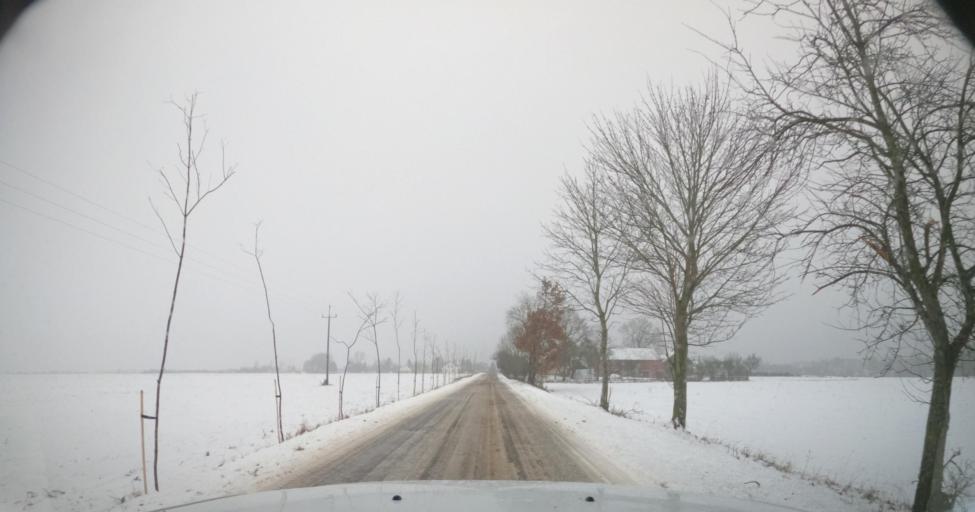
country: PL
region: West Pomeranian Voivodeship
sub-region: Powiat kamienski
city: Golczewo
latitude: 53.8061
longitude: 14.9663
